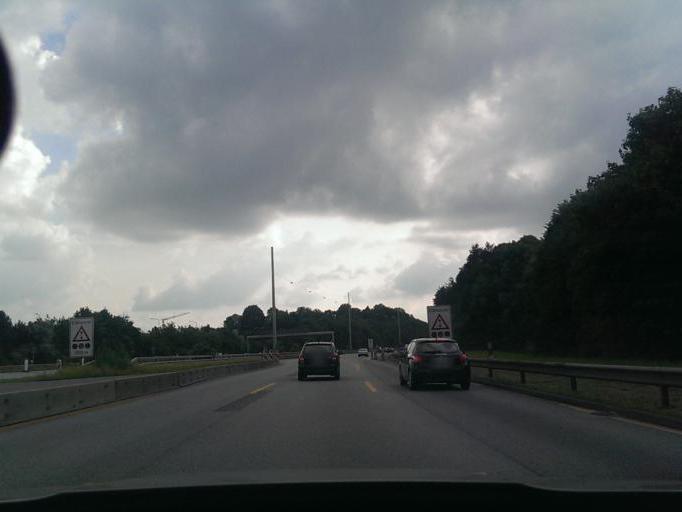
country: DE
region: Hamburg
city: Stellingen
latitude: 53.5796
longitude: 9.9138
